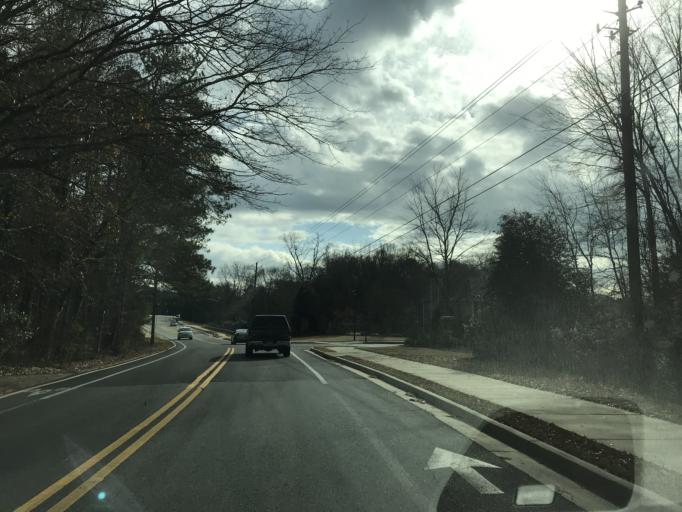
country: US
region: Georgia
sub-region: Fulton County
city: Alpharetta
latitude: 34.0887
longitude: -84.3105
